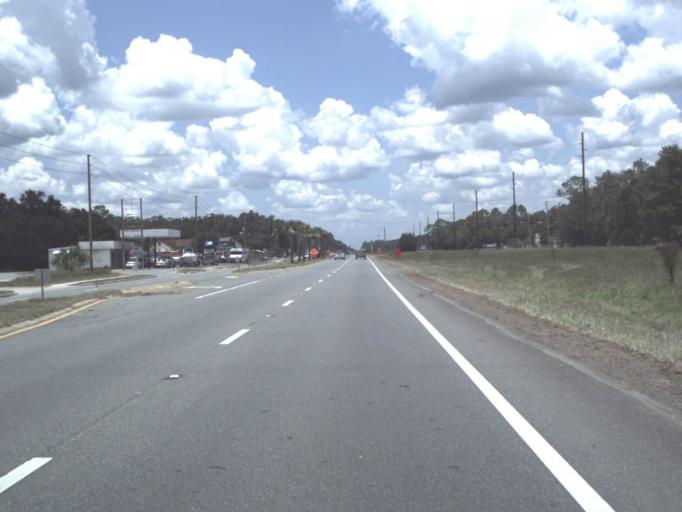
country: US
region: Florida
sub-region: Taylor County
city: Perry
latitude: 30.1220
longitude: -83.5925
